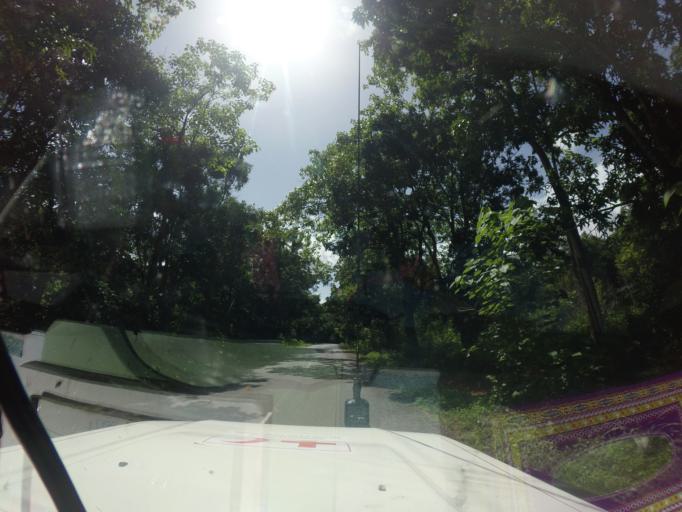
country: GN
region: Mamou
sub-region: Mamou Prefecture
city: Mamou
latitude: 10.2531
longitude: -11.8868
